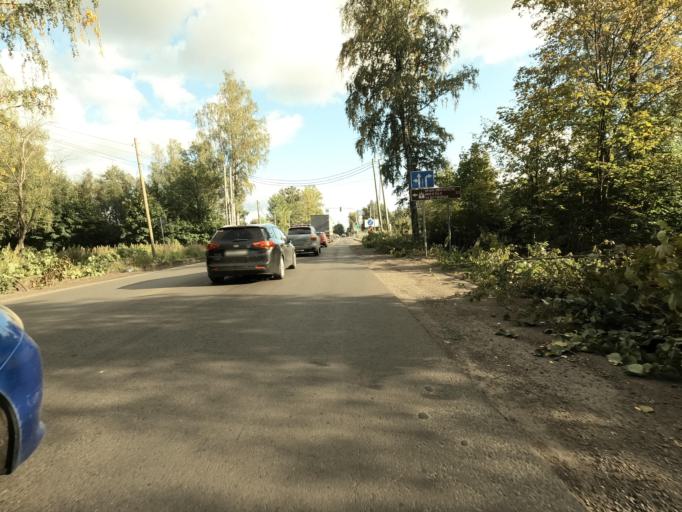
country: RU
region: Leningrad
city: Koltushi
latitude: 59.9380
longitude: 30.6610
